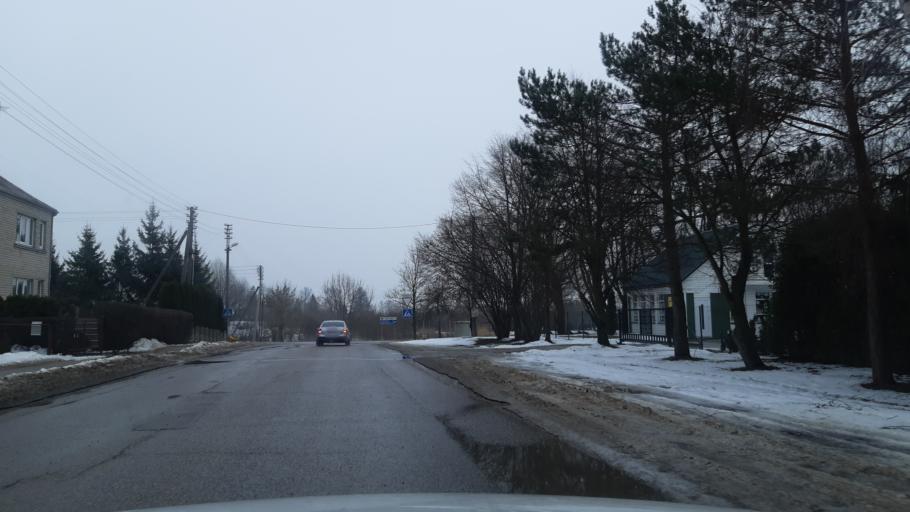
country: LT
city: Vilkaviskis
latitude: 54.6442
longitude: 23.0190
